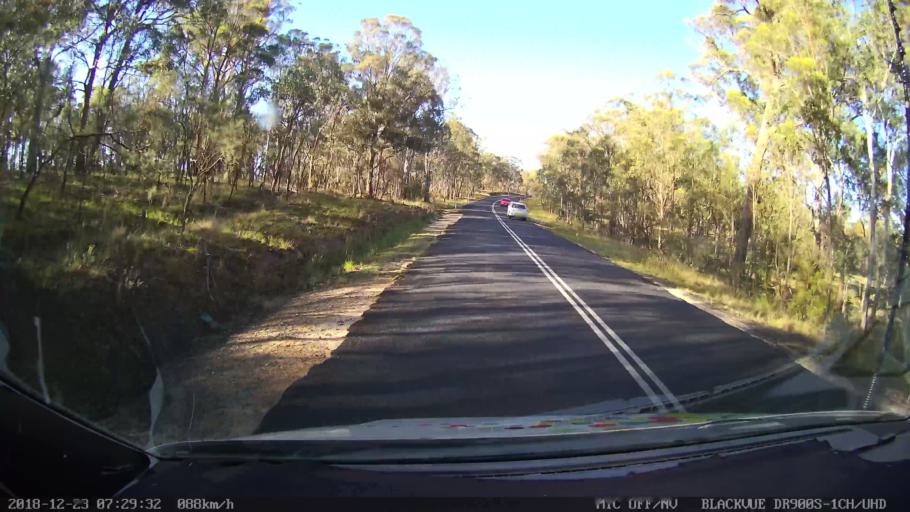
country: AU
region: New South Wales
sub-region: Armidale Dumaresq
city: Enmore
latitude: -30.4958
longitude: 152.1551
